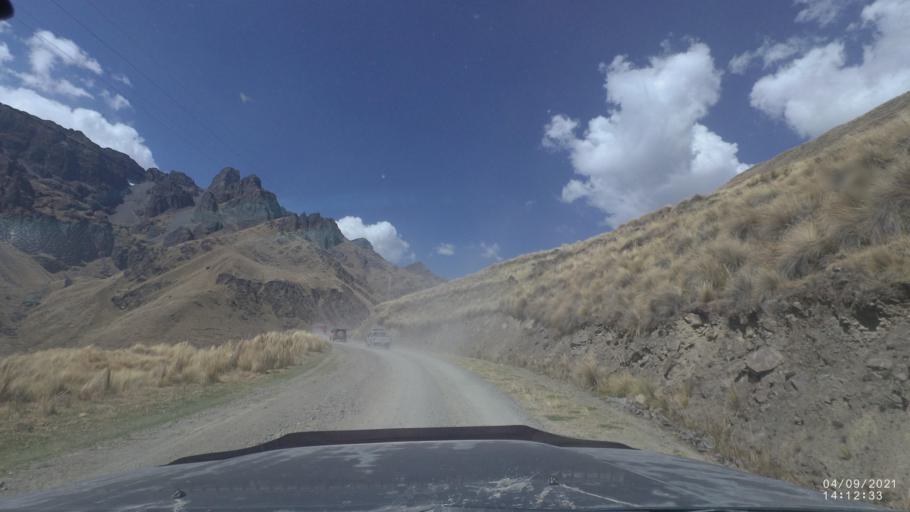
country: BO
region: Cochabamba
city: Sipe Sipe
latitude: -17.2242
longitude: -66.4513
